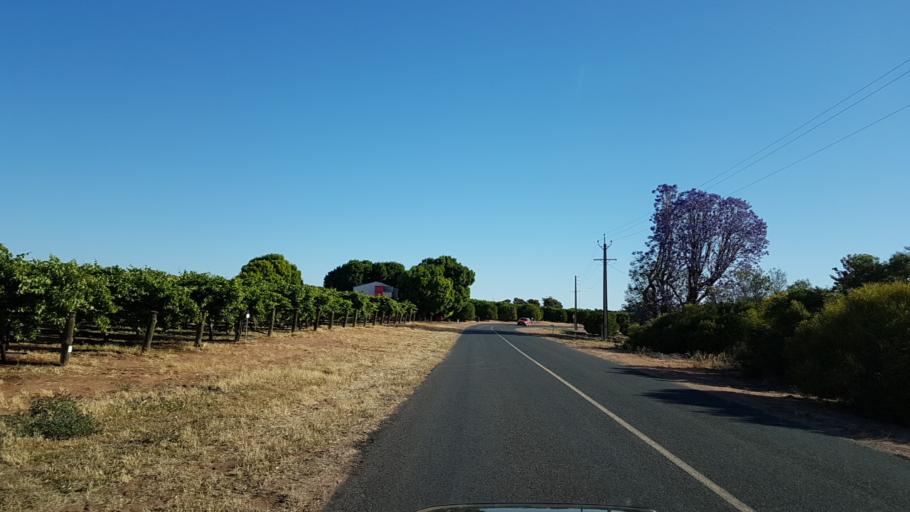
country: AU
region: South Australia
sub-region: Loxton Waikerie
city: Waikerie
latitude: -34.1732
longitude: 140.0307
